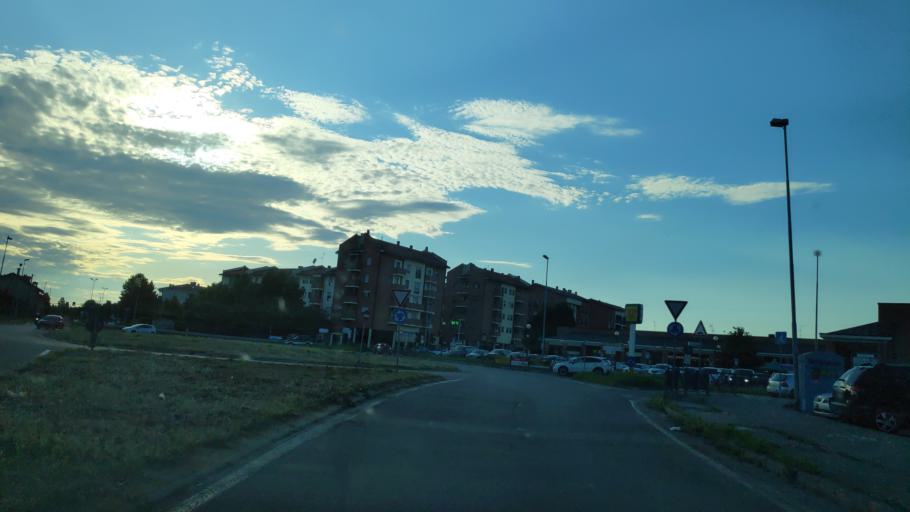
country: IT
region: Lombardy
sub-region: Citta metropolitana di Milano
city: Vigliano-Bettolino
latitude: 45.4327
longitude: 9.3418
